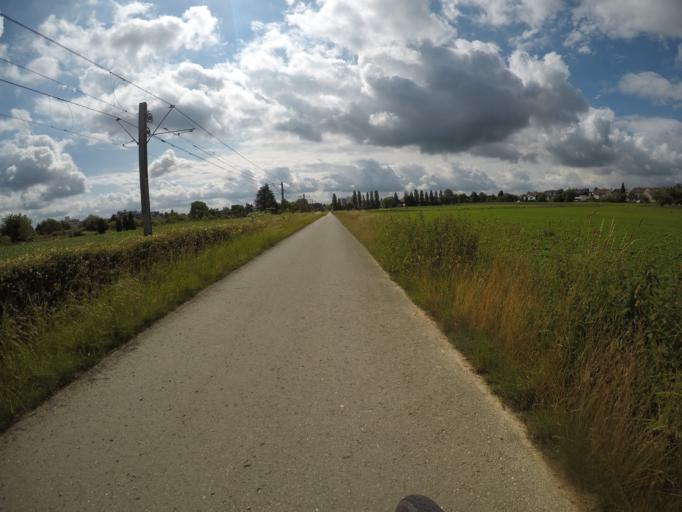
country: DE
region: Baden-Wuerttemberg
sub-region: Regierungsbezirk Stuttgart
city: Ostfildern
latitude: 48.7349
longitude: 9.2465
